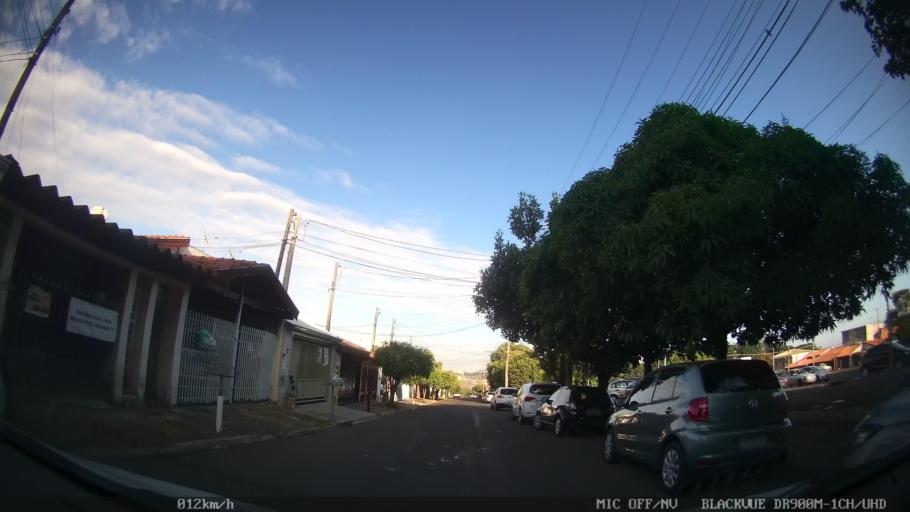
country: BR
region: Sao Paulo
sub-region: Santa Barbara D'Oeste
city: Santa Barbara d'Oeste
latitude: -22.7475
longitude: -47.3774
